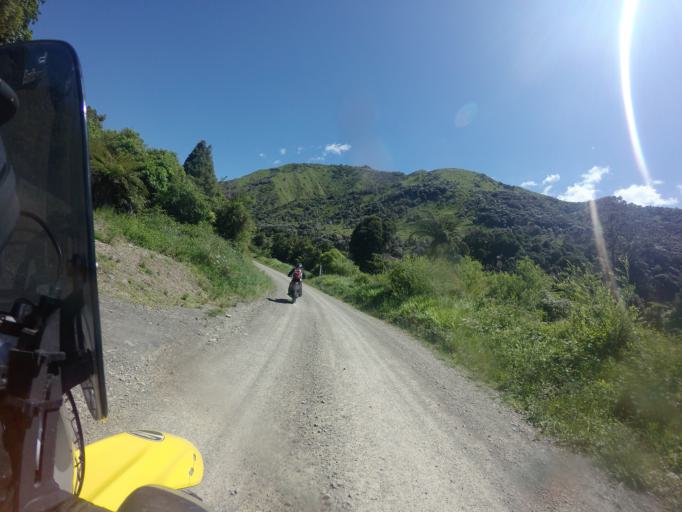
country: NZ
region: Bay of Plenty
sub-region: Opotiki District
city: Opotiki
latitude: -38.2776
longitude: 177.3418
